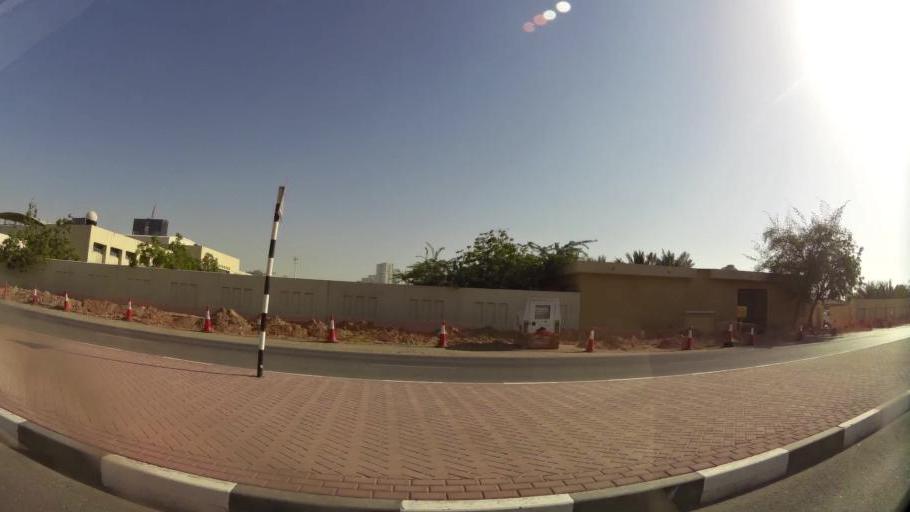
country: AE
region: Ajman
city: Ajman
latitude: 25.4023
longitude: 55.4730
